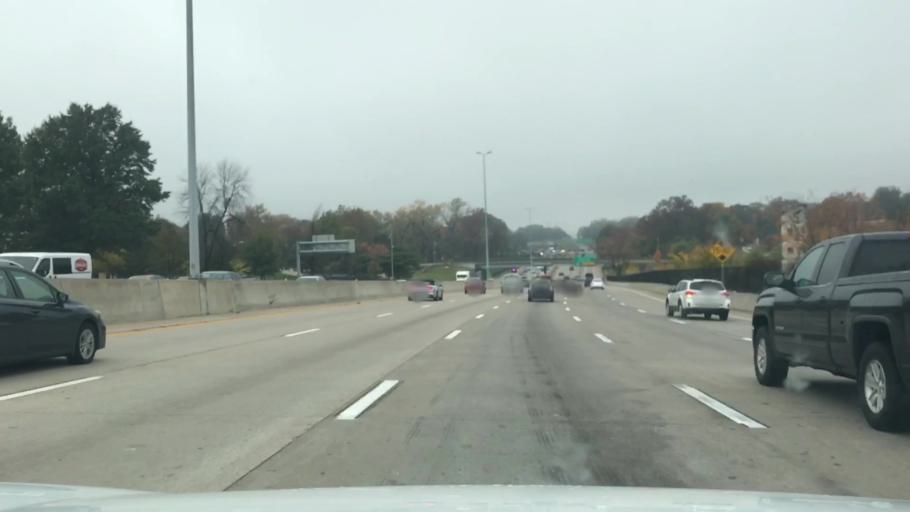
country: US
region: Missouri
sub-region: Saint Louis County
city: Richmond Heights
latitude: 38.6321
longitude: -90.2903
